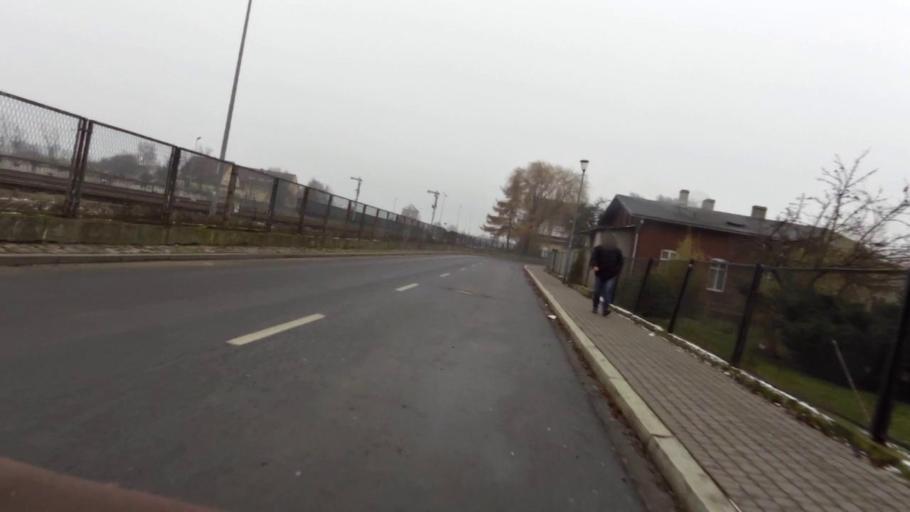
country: PL
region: West Pomeranian Voivodeship
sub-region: Powiat walecki
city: Walcz
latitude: 53.2762
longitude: 16.4836
